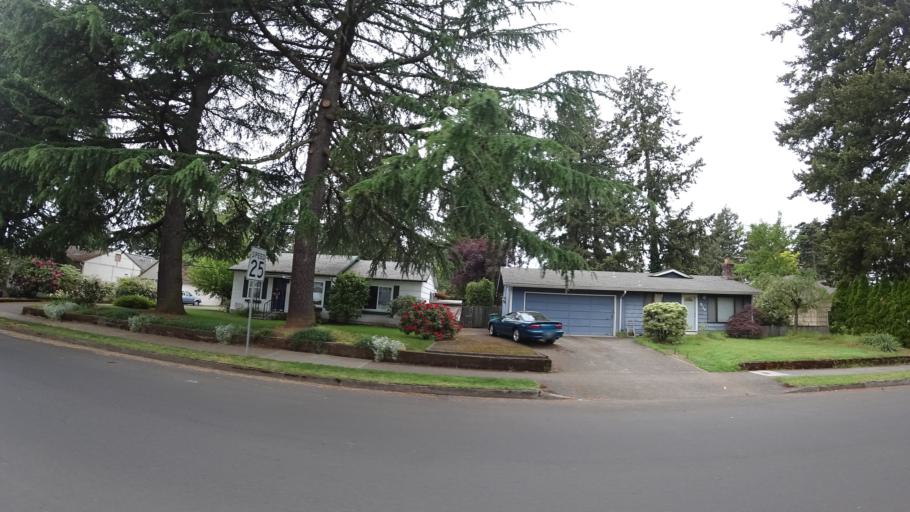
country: US
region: Oregon
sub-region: Multnomah County
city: Lents
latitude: 45.5076
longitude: -122.5299
